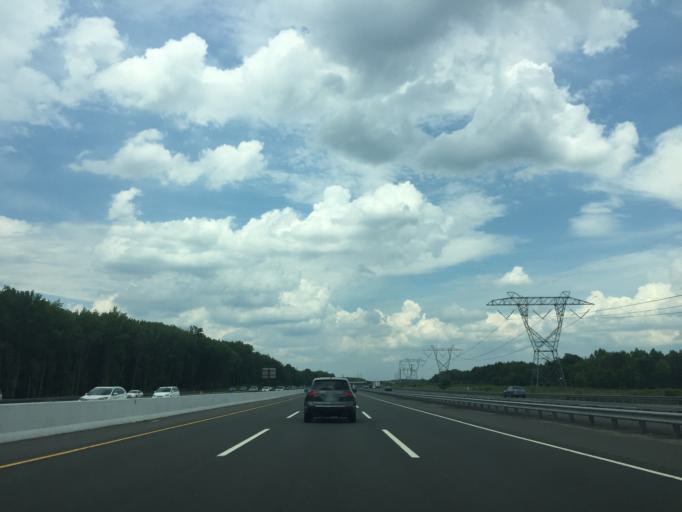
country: US
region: New Jersey
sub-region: Monmouth County
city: Shrewsbury
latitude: 40.2273
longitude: -74.5519
